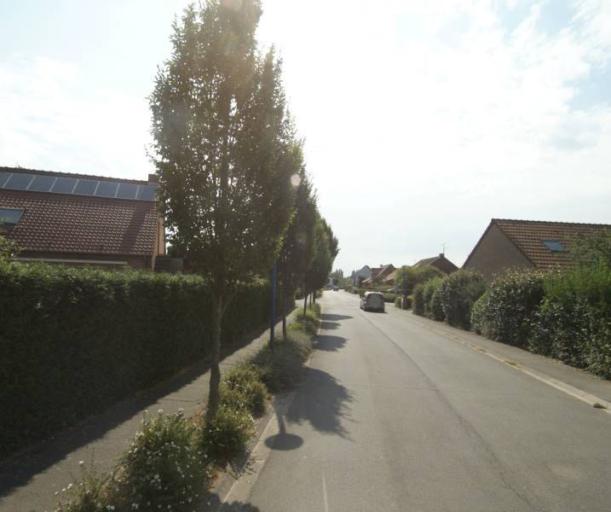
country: FR
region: Nord-Pas-de-Calais
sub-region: Departement du Nord
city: Sainghin-en-Weppes
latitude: 50.5658
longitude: 2.8981
